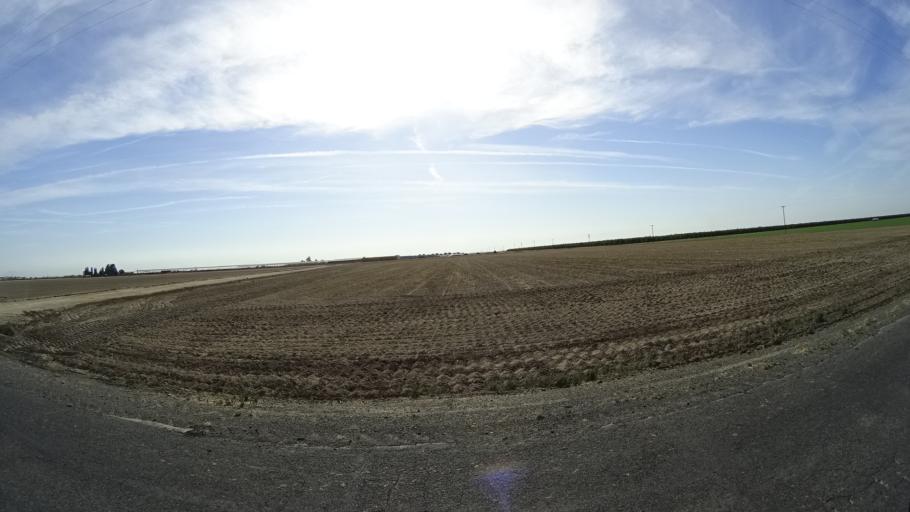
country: US
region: California
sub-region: Kings County
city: Lucerne
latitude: 36.3952
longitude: -119.5469
